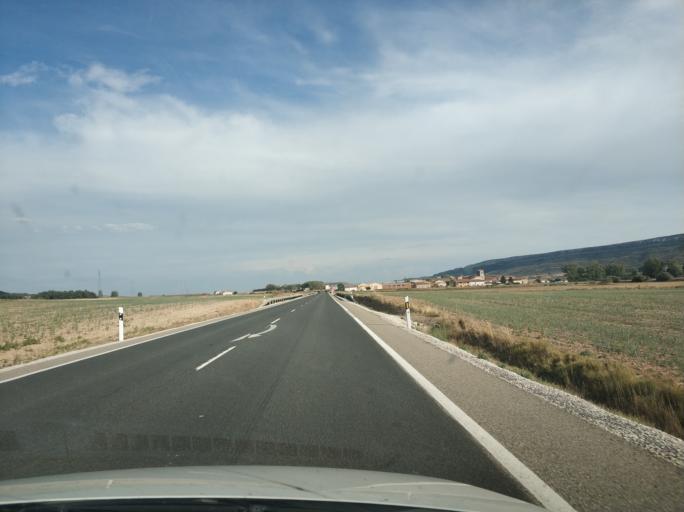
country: ES
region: Castille and Leon
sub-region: Provincia de Palencia
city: Pomar de Valdivia
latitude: 42.7437
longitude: -4.1549
